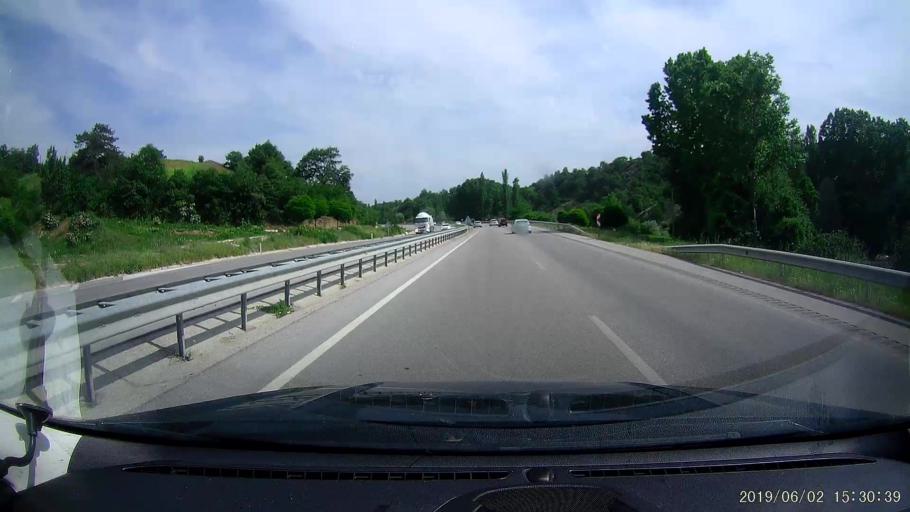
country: TR
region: Amasya
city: Saraycik
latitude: 40.9518
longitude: 35.1134
